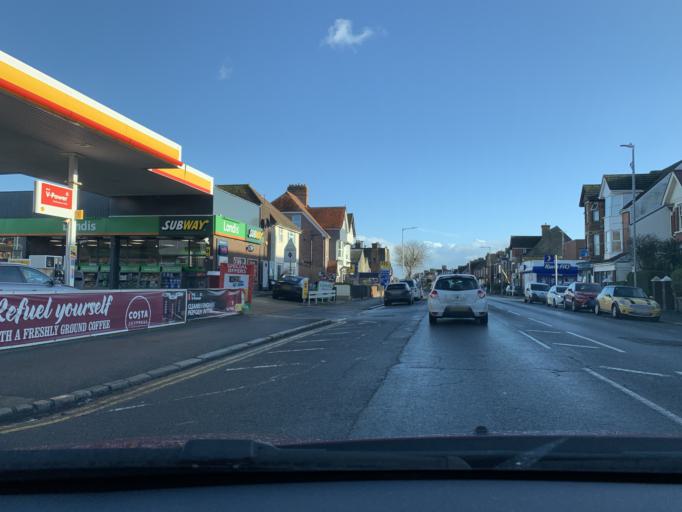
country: GB
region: England
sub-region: Kent
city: Hawkinge
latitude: 51.0870
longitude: 1.1493
